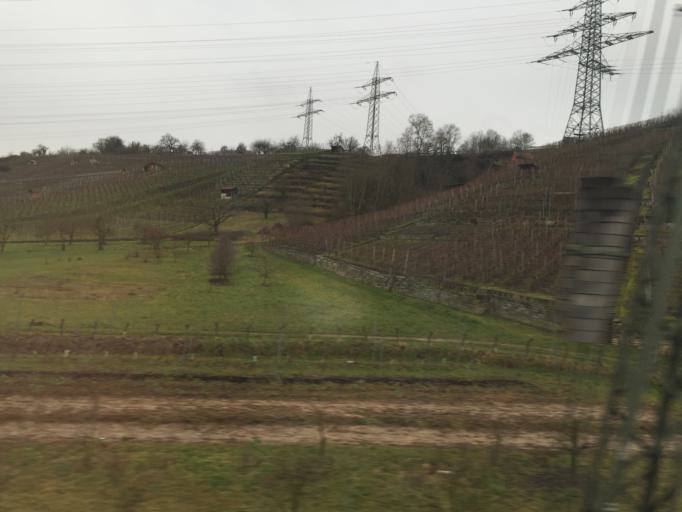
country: DE
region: Baden-Wuerttemberg
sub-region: Regierungsbezirk Stuttgart
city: Gemmrigheim
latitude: 49.0215
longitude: 9.1539
